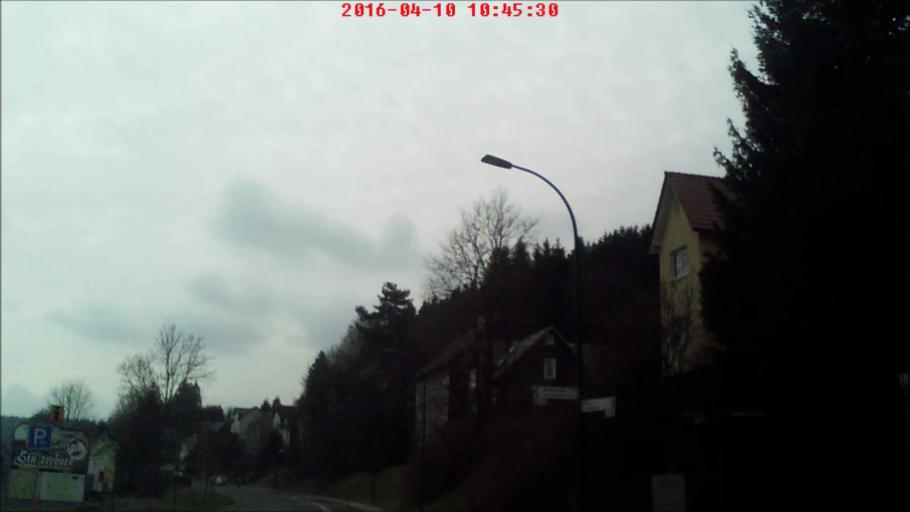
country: DE
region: Thuringia
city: Stutzerbach
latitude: 50.6414
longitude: 10.8560
